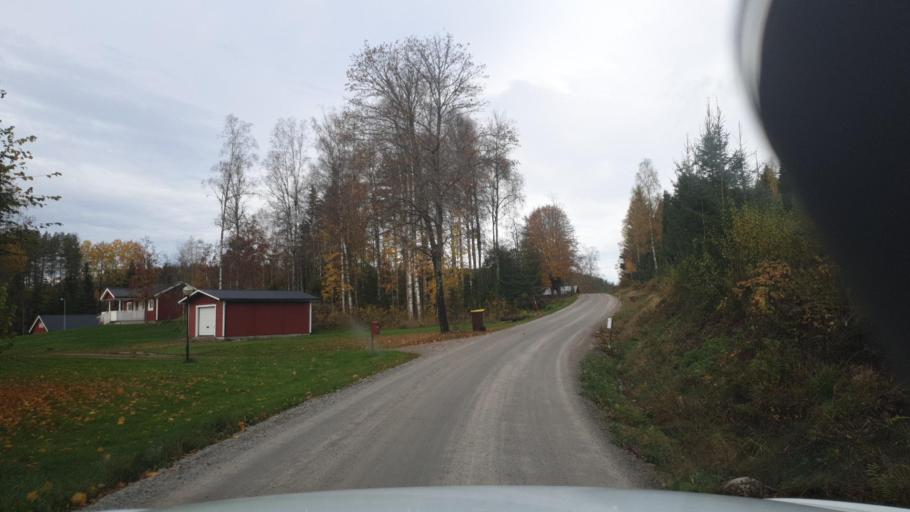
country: SE
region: Vaermland
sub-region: Sunne Kommun
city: Sunne
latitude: 59.7068
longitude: 12.8799
